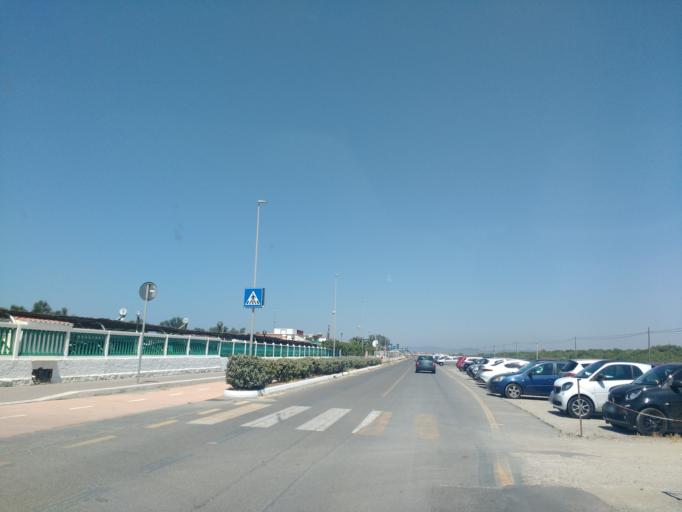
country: IT
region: Latium
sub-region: Citta metropolitana di Roma Capitale
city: Passo Oscuro
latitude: 41.8811
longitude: 12.1739
